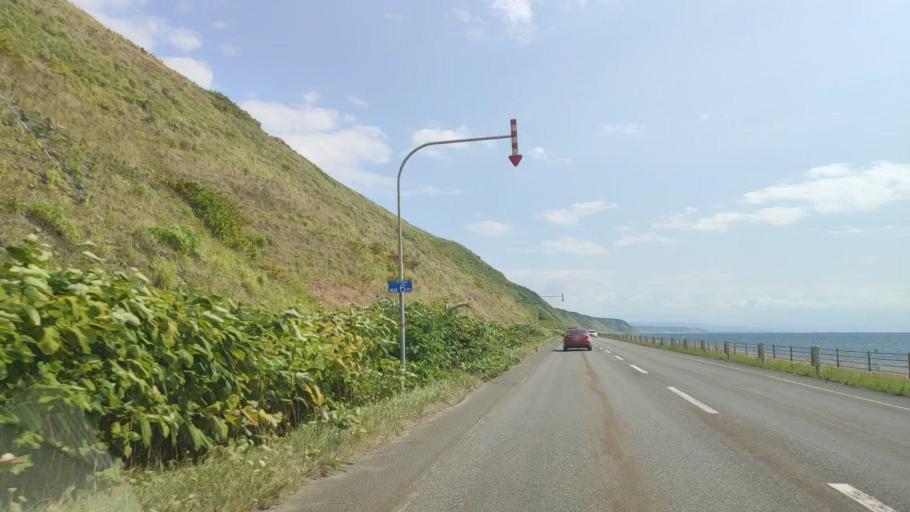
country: JP
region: Hokkaido
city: Rumoi
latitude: 44.0659
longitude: 141.6630
